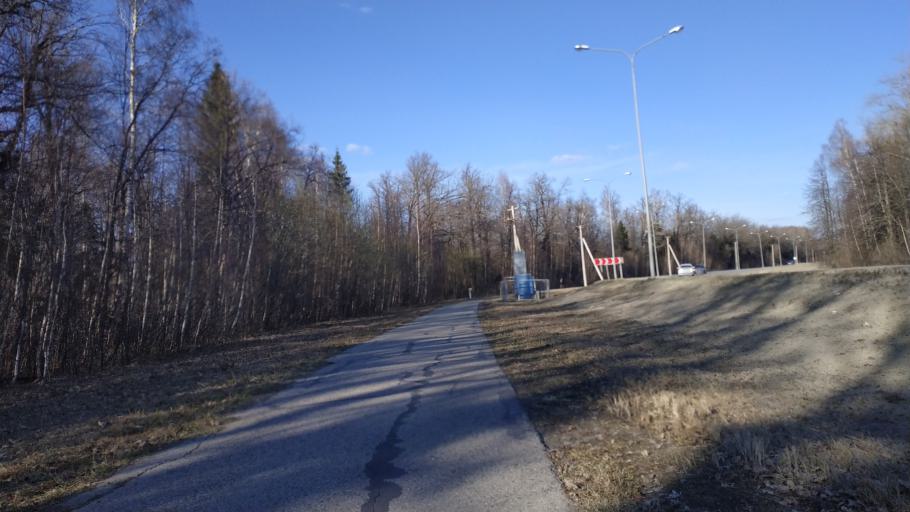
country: RU
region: Chuvashia
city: Ishley
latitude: 56.1309
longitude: 47.0728
